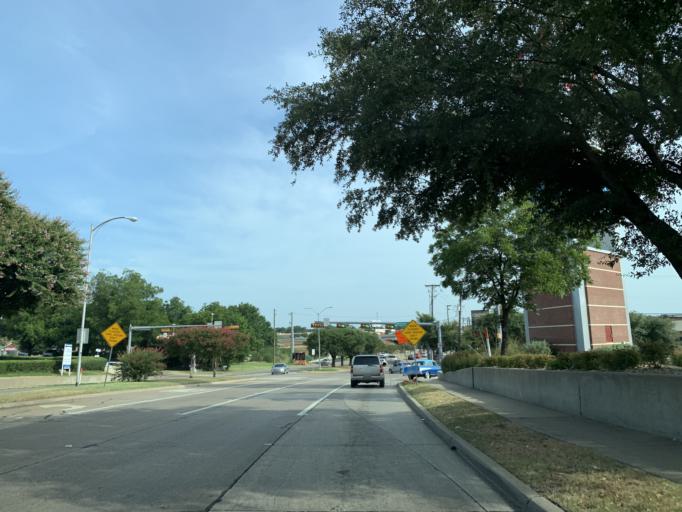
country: US
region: Texas
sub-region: Dallas County
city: Grand Prairie
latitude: 32.6728
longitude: -97.0065
